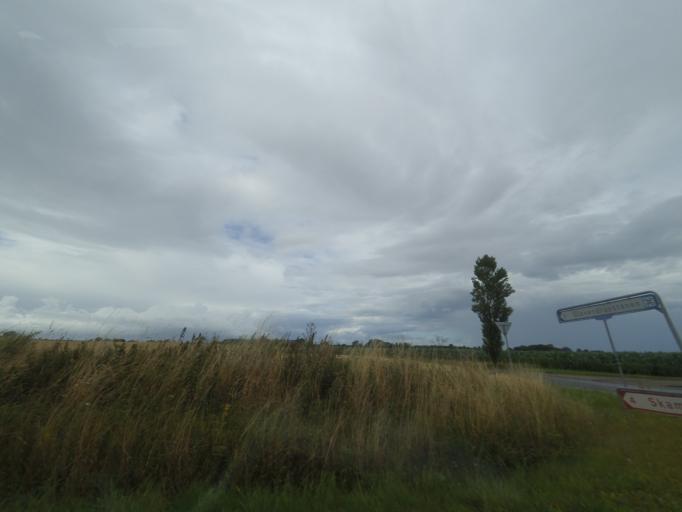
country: DK
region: South Denmark
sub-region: Nordfyns Kommune
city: Sonderso
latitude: 55.4918
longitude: 10.2856
